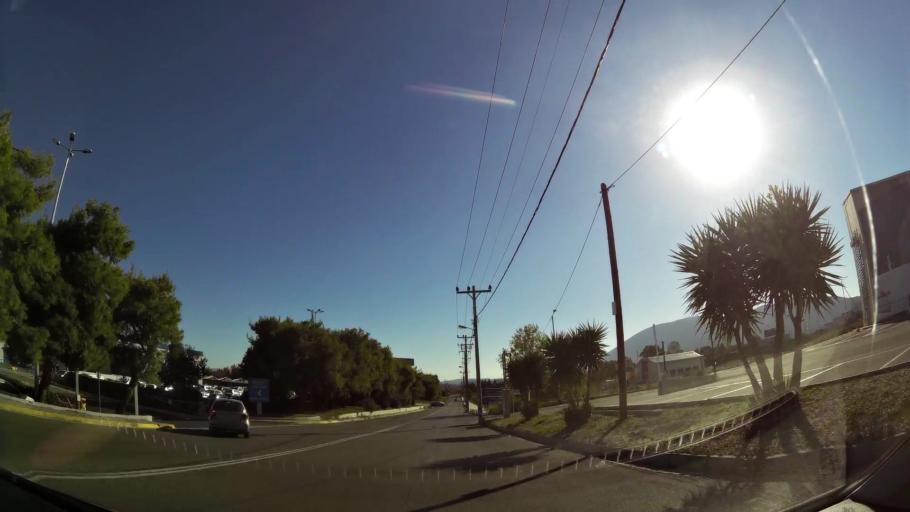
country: GR
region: Attica
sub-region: Nomarchia Anatolikis Attikis
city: Anthousa
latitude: 38.0152
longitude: 23.8717
